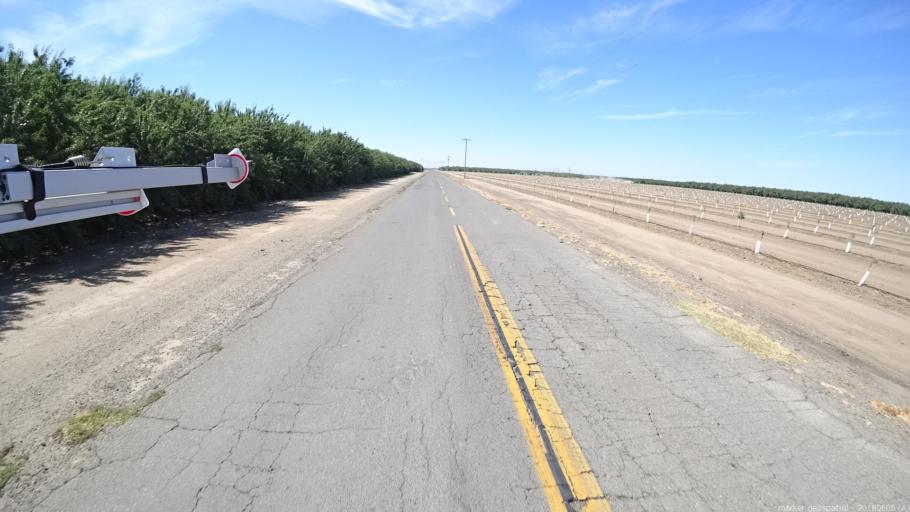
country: US
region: California
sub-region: Madera County
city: Chowchilla
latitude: 37.0249
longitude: -120.3833
